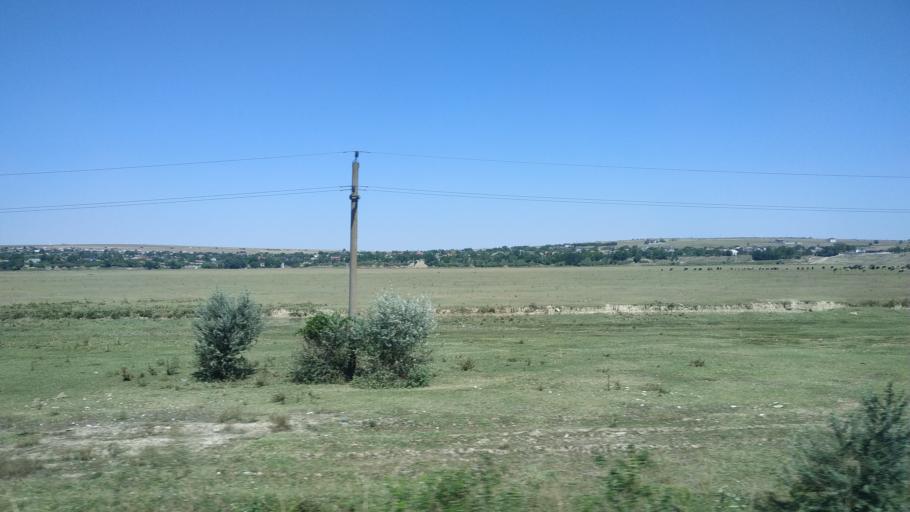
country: RO
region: Constanta
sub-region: Comuna Mircea Voda
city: Satu Nou
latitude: 44.2580
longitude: 28.2256
